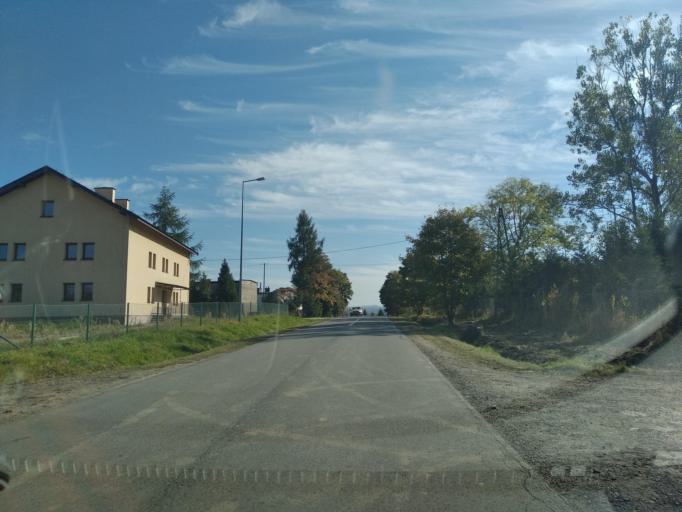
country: PL
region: Subcarpathian Voivodeship
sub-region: Powiat sanocki
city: Komancza
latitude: 49.3692
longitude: 22.0033
